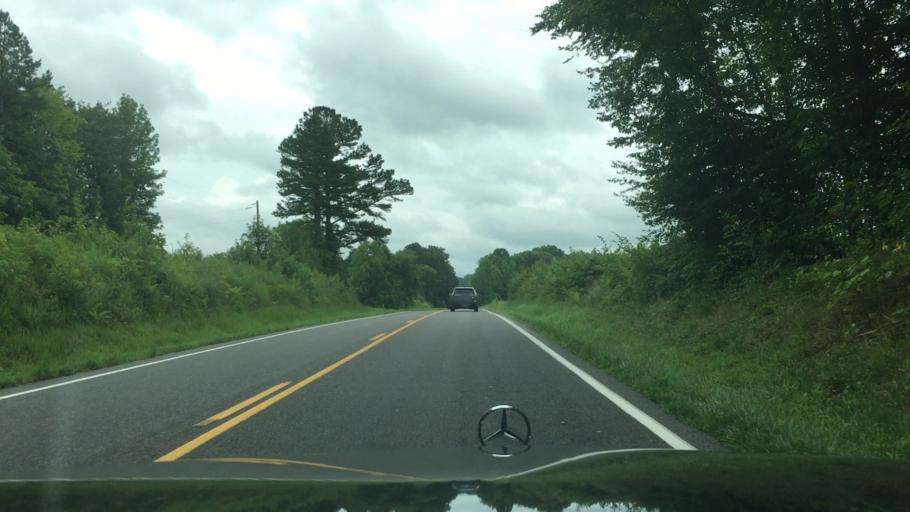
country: US
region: Virginia
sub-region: Nottoway County
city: Crewe
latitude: 37.2779
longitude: -78.1847
